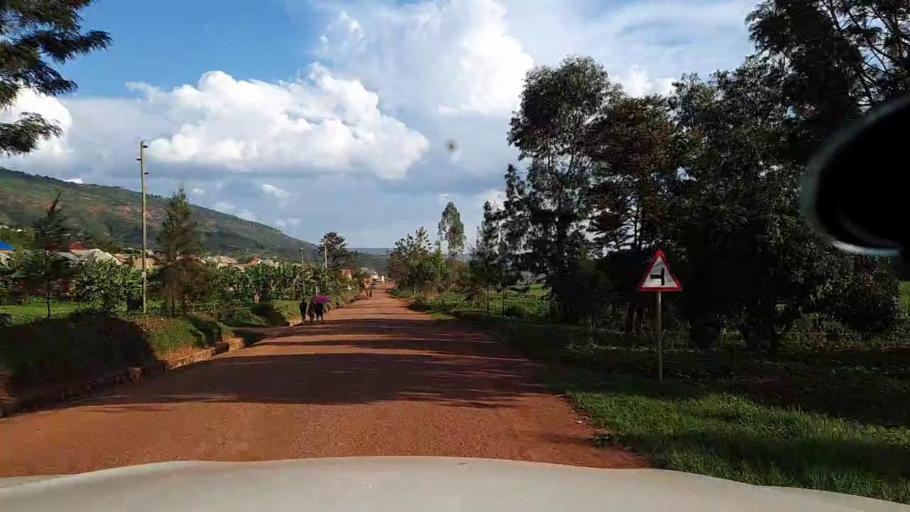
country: RW
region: Kigali
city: Kigali
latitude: -1.9084
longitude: 29.9807
